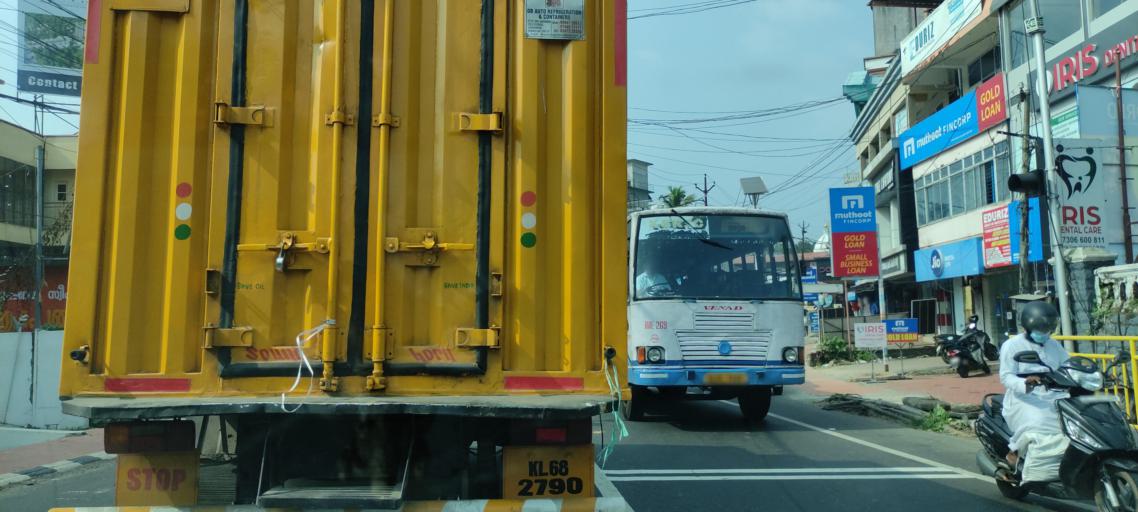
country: IN
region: Kerala
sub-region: Alappuzha
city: Chengannur
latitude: 9.3146
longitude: 76.6176
